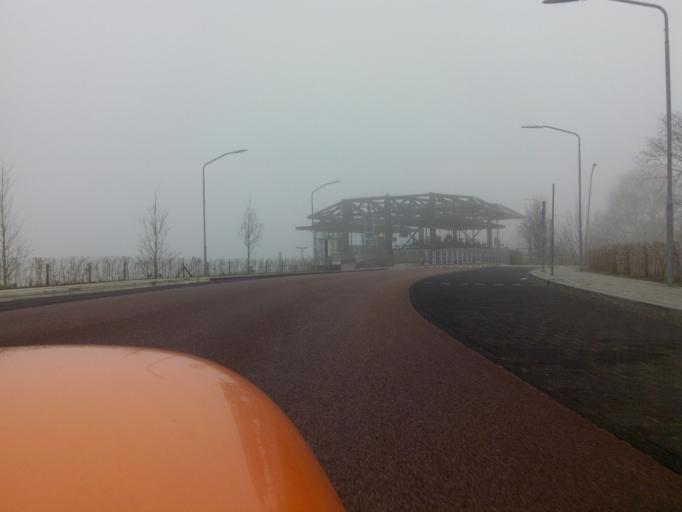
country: NL
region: Utrecht
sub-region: Gemeente Leusden
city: Leusden
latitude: 52.1657
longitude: 5.4584
